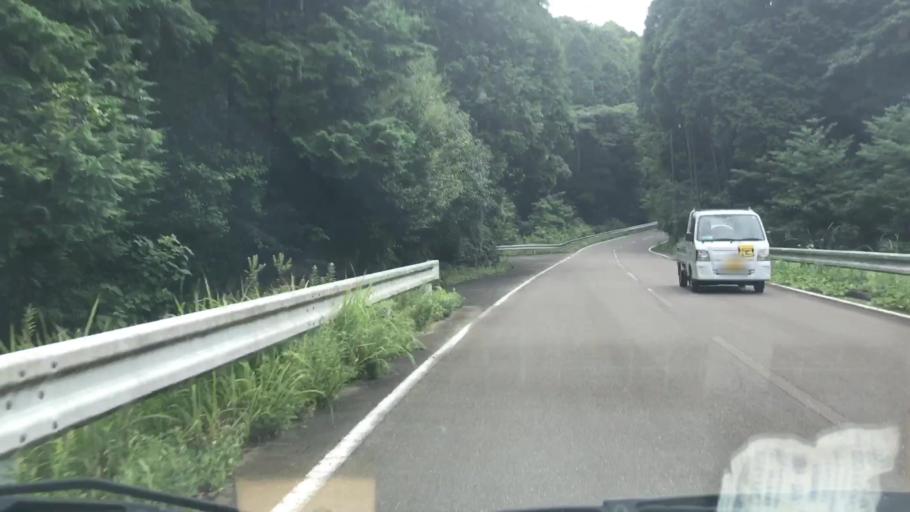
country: JP
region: Saga Prefecture
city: Takeocho-takeo
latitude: 33.2271
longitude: 129.9961
